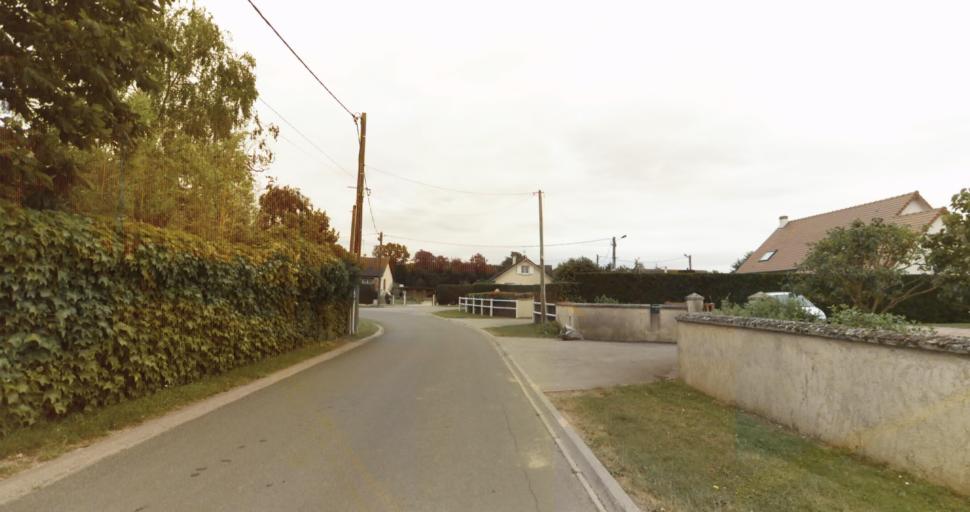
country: FR
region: Haute-Normandie
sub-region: Departement de l'Eure
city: Evreux
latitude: 48.9733
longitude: 1.2348
